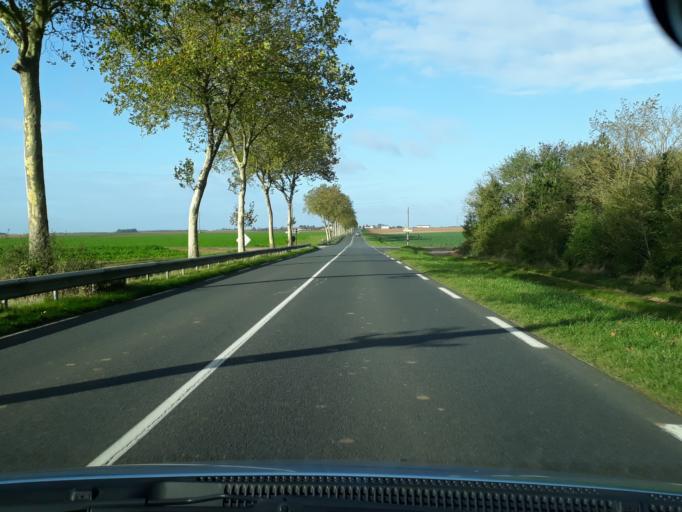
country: FR
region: Ile-de-France
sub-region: Departement de Seine-et-Marne
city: Noisy-sur-Ecole
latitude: 48.3054
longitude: 2.4995
